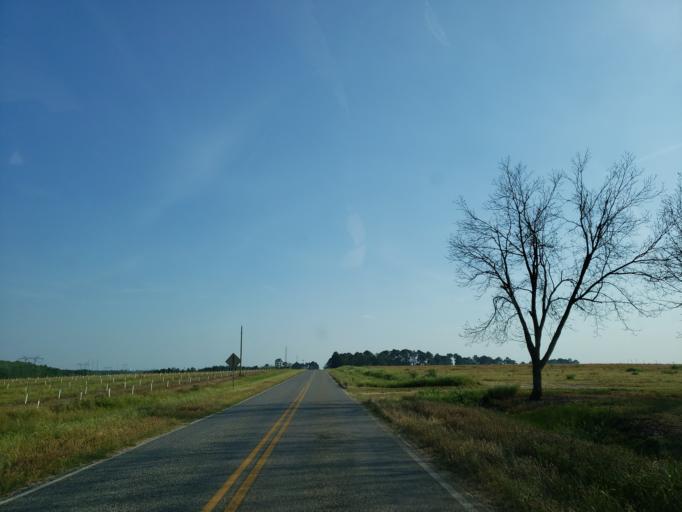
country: US
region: Georgia
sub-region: Tift County
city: Tifton
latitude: 31.5168
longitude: -83.5600
